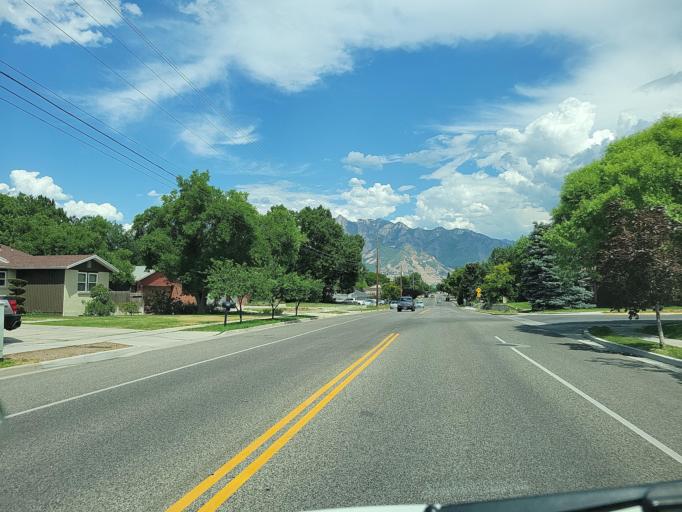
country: US
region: Utah
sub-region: Salt Lake County
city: Murray
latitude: 40.6417
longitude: -111.8769
